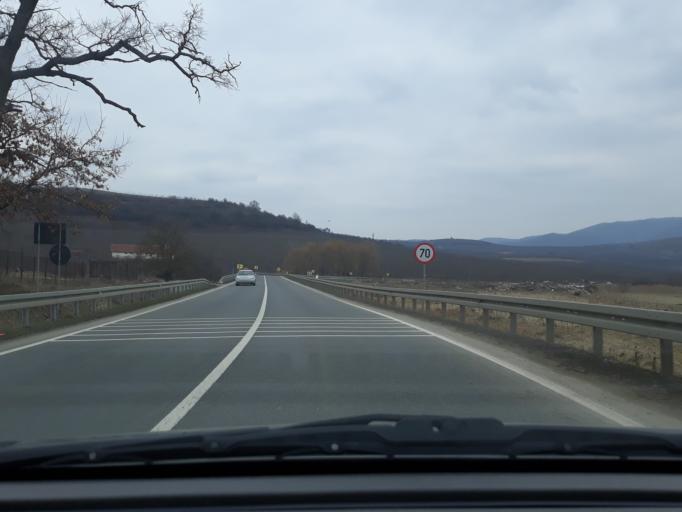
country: RO
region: Salaj
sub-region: Comuna Nusfalau
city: Nusfalau
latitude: 47.2202
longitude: 22.7475
